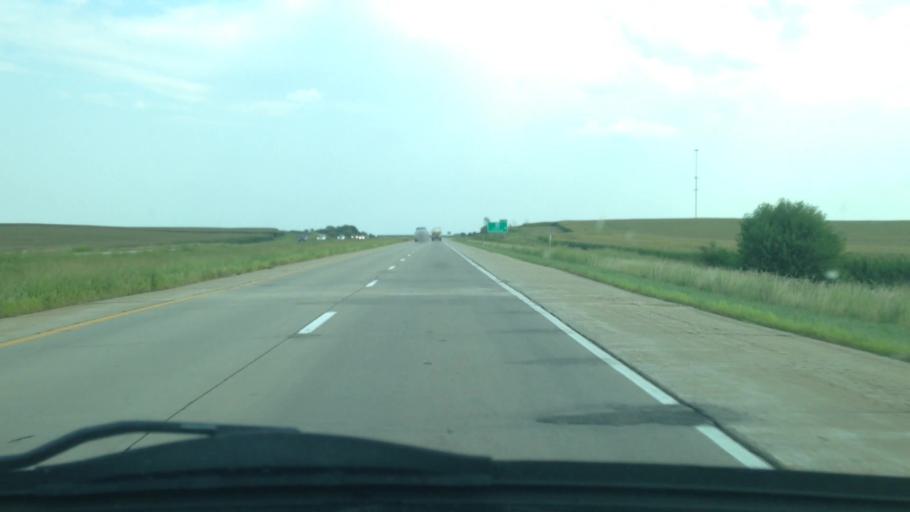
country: US
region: Iowa
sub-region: Buchanan County
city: Jesup
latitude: 42.3576
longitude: -92.0749
